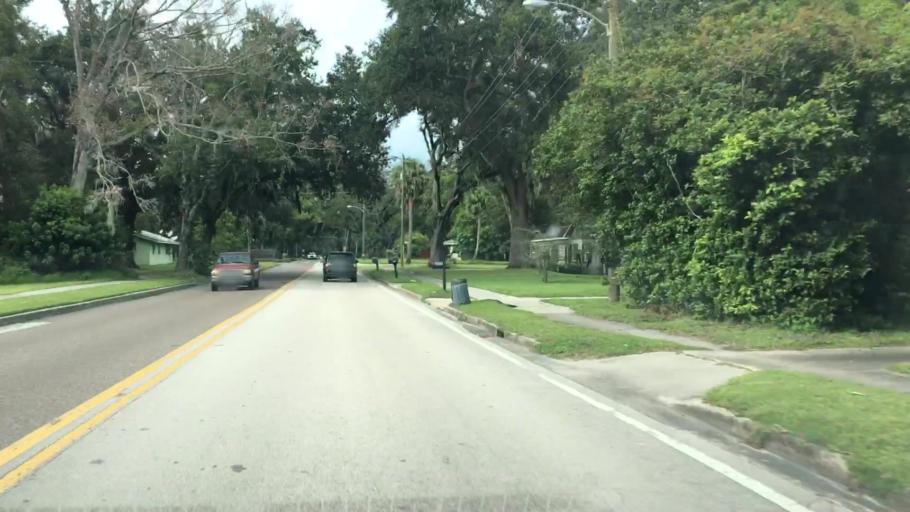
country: US
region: Florida
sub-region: Seminole County
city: Sanford
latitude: 28.7892
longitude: -81.2648
